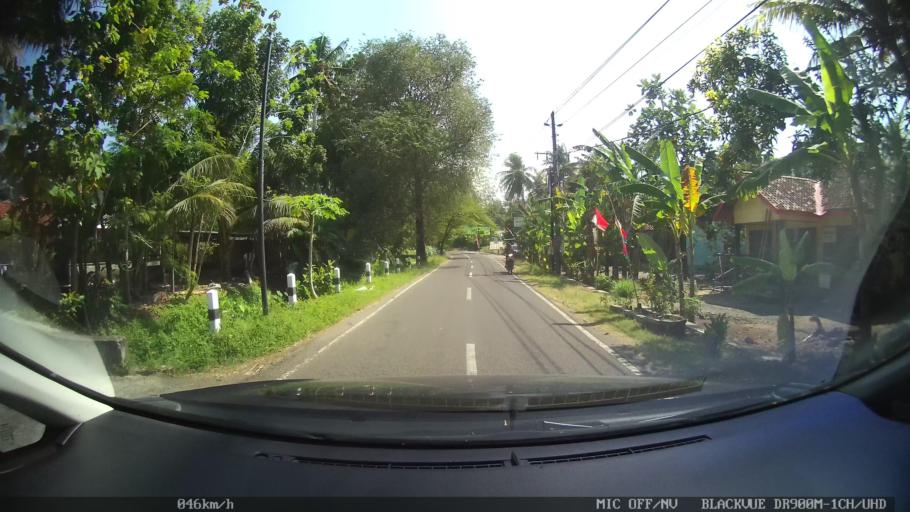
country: ID
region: Daerah Istimewa Yogyakarta
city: Srandakan
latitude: -7.9217
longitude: 110.1574
